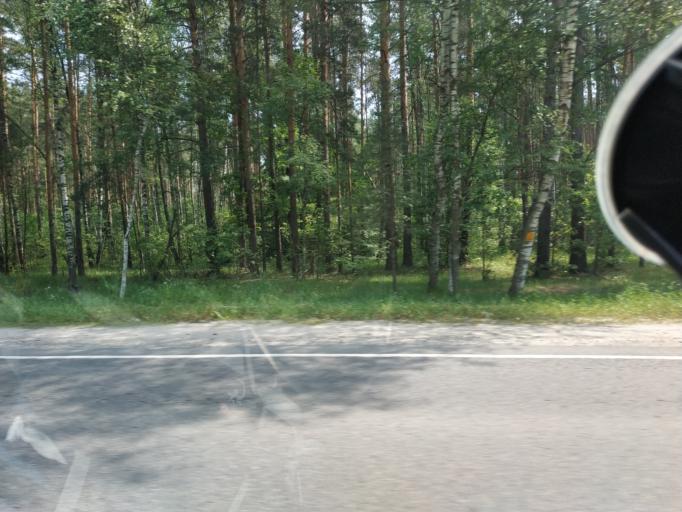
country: RU
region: Moskovskaya
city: Malyshevo
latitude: 55.5228
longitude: 38.3441
